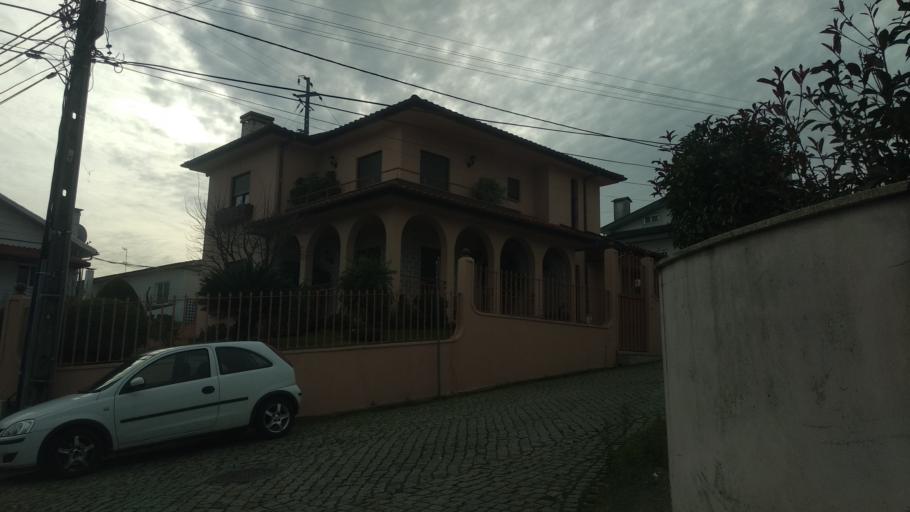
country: PT
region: Braga
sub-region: Braga
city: Braga
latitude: 41.5263
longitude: -8.4399
